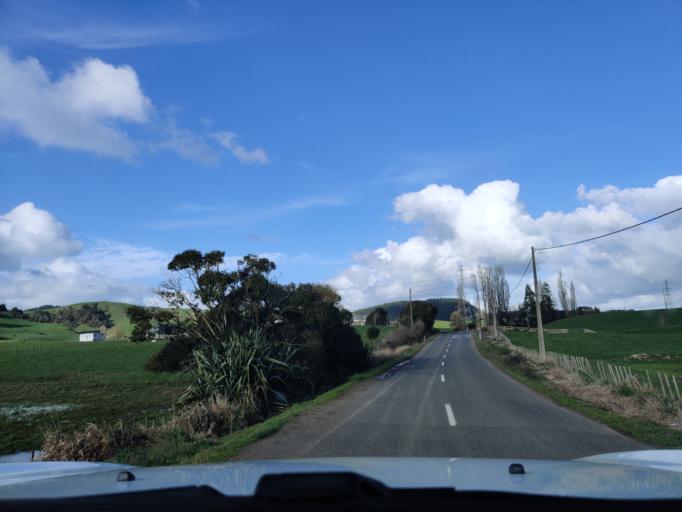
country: NZ
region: Waikato
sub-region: Waikato District
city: Te Kauwhata
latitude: -37.2858
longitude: 175.2151
